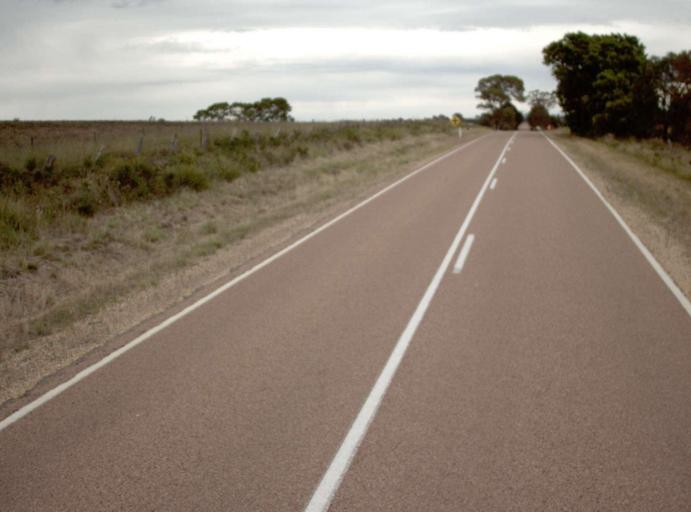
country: AU
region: Victoria
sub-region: East Gippsland
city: Bairnsdale
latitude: -37.9978
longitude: 147.3606
